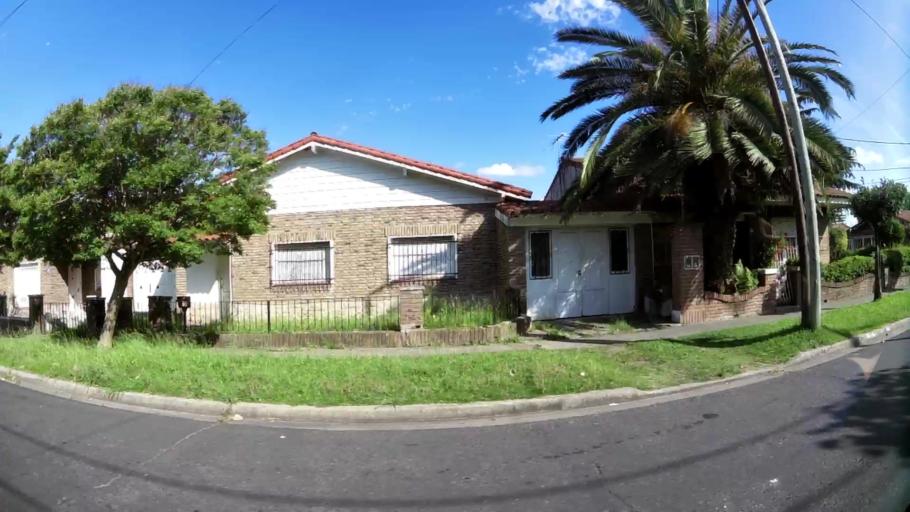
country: AR
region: Buenos Aires
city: San Justo
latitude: -34.6679
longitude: -58.5859
